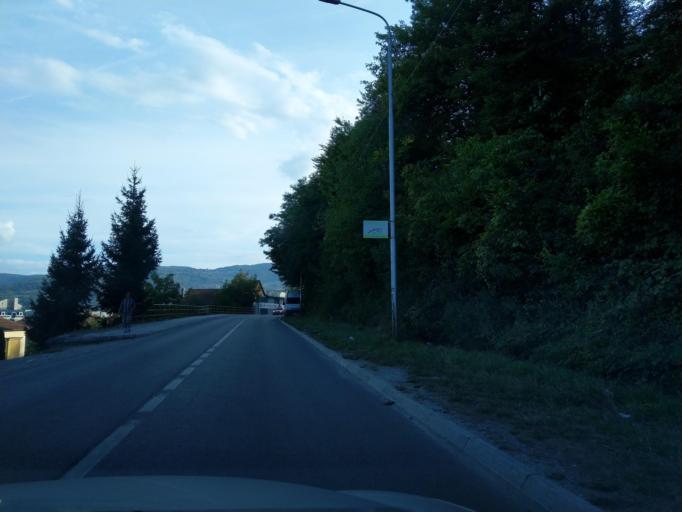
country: RS
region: Central Serbia
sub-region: Zlatiborski Okrug
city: Prijepolje
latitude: 43.3569
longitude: 19.6355
